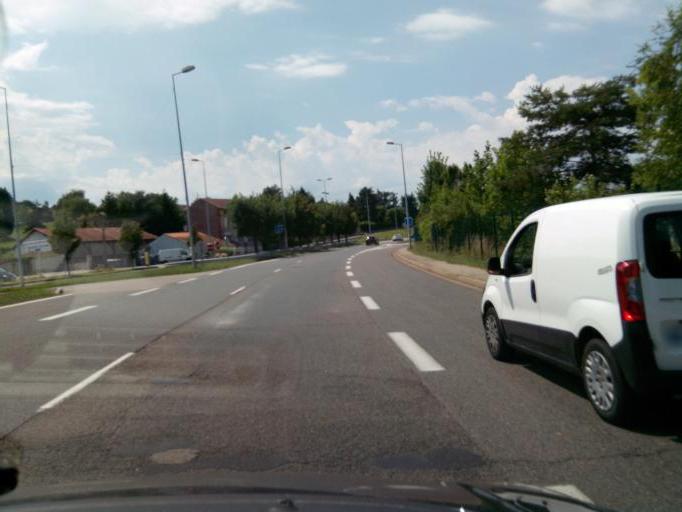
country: FR
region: Rhone-Alpes
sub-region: Departement de la Loire
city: Roche-la-Moliere
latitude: 45.4328
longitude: 4.3318
